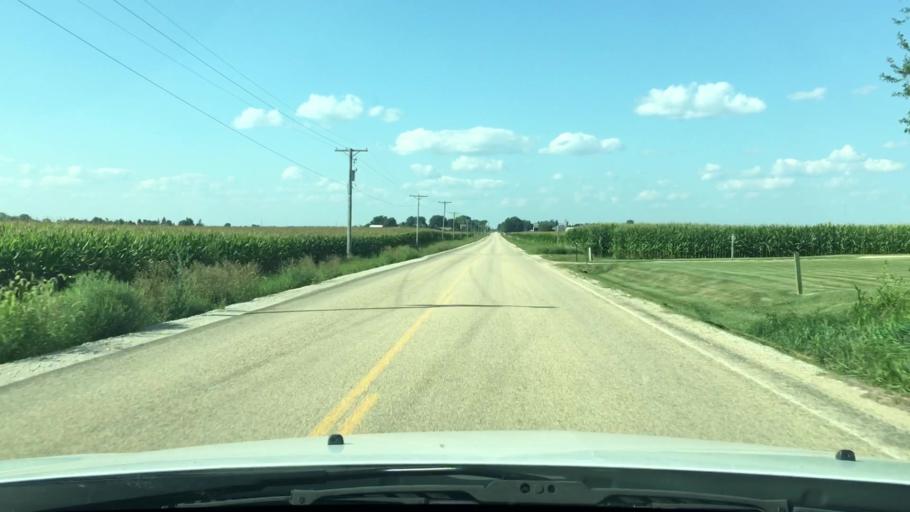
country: US
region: Illinois
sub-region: DeKalb County
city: Waterman
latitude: 41.8381
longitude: -88.7734
